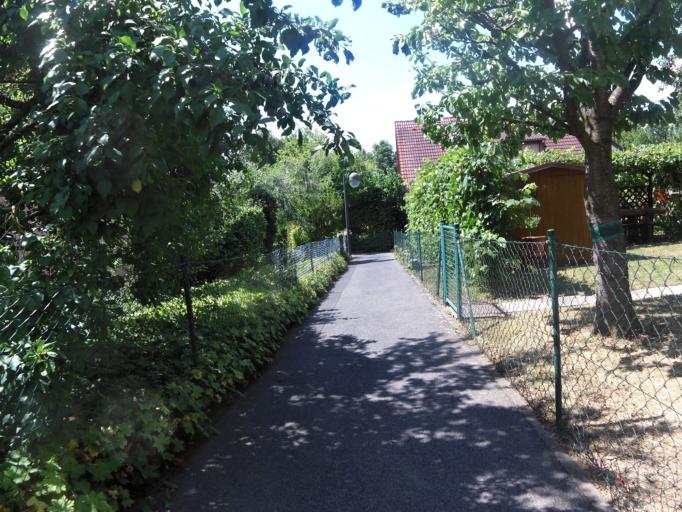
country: DE
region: Bavaria
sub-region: Regierungsbezirk Unterfranken
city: Randersacker
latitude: 49.7370
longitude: 9.9562
